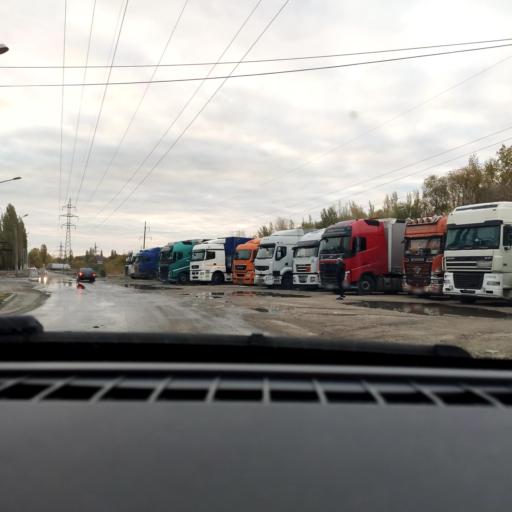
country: RU
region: Voronezj
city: Maslovka
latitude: 51.6238
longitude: 39.2462
